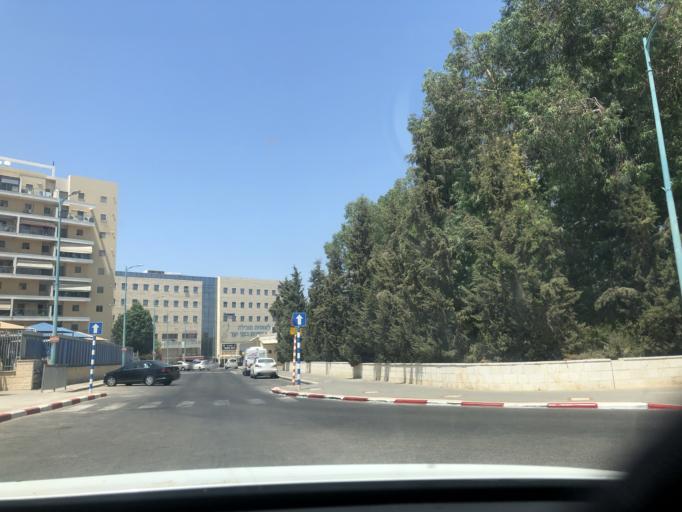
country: IL
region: Central District
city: Lod
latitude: 31.9436
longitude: 34.9012
